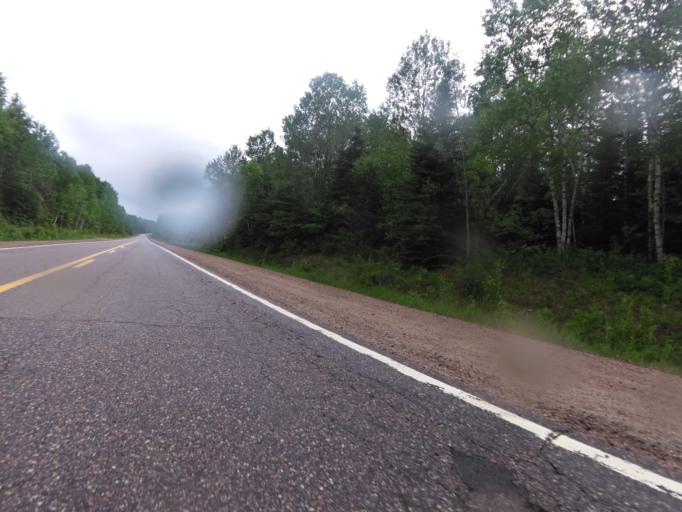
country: CA
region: Quebec
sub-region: Outaouais
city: Shawville
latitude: 45.9101
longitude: -76.2612
